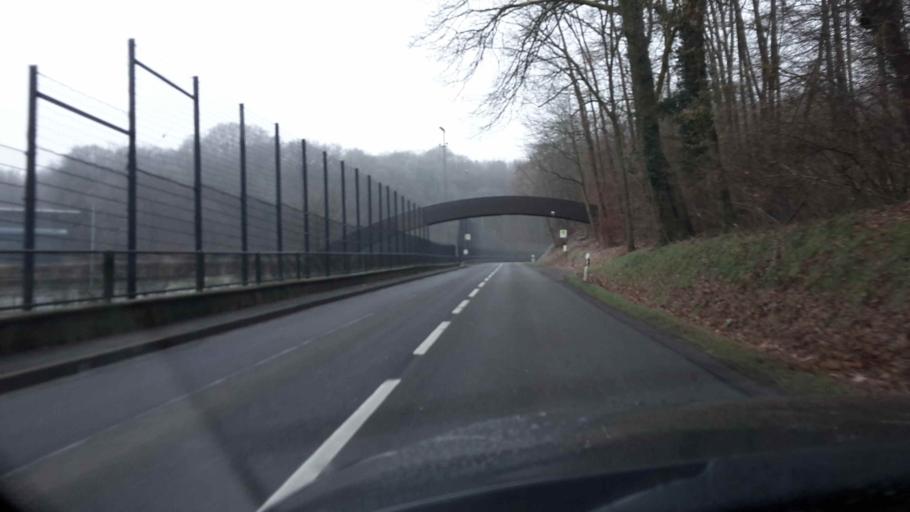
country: DE
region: North Rhine-Westphalia
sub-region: Regierungsbezirk Koln
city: Hennef
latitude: 50.7617
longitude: 7.2730
